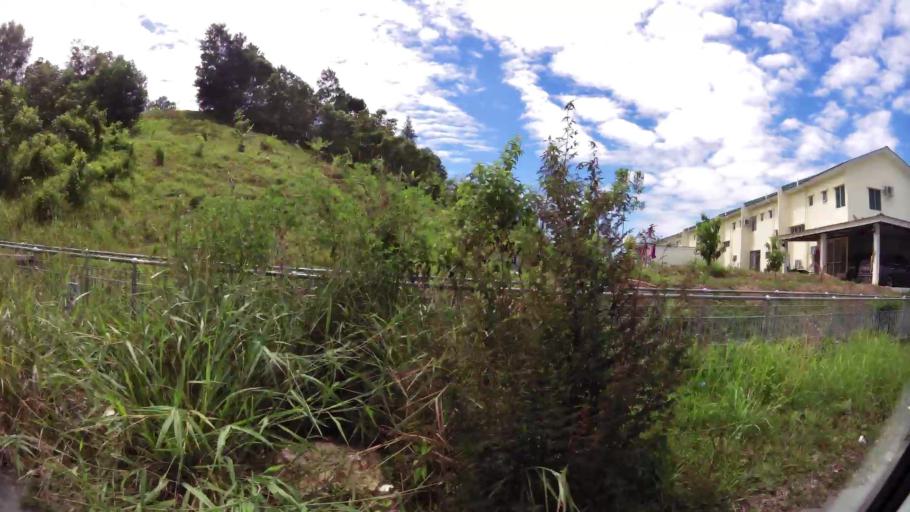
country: BN
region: Brunei and Muara
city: Bandar Seri Begawan
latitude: 4.9775
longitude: 115.0136
